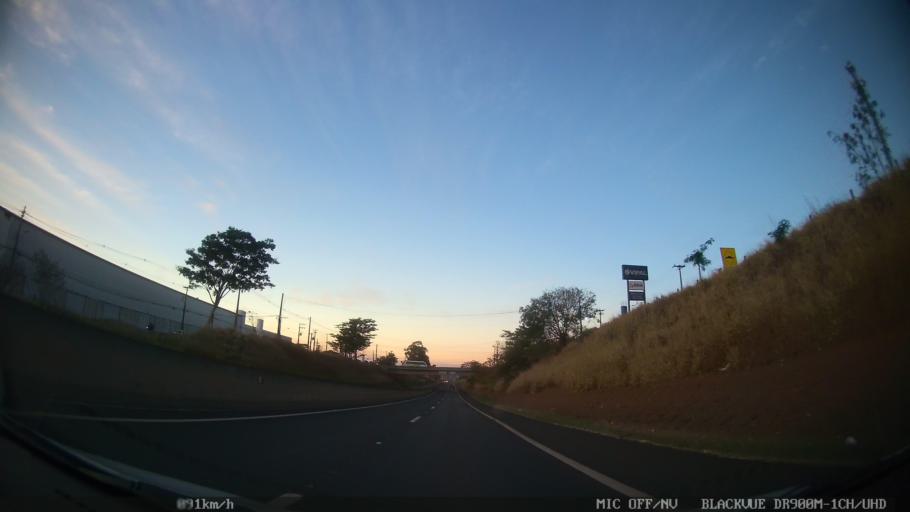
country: BR
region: Sao Paulo
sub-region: Catanduva
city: Catanduva
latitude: -21.1283
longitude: -49.0078
